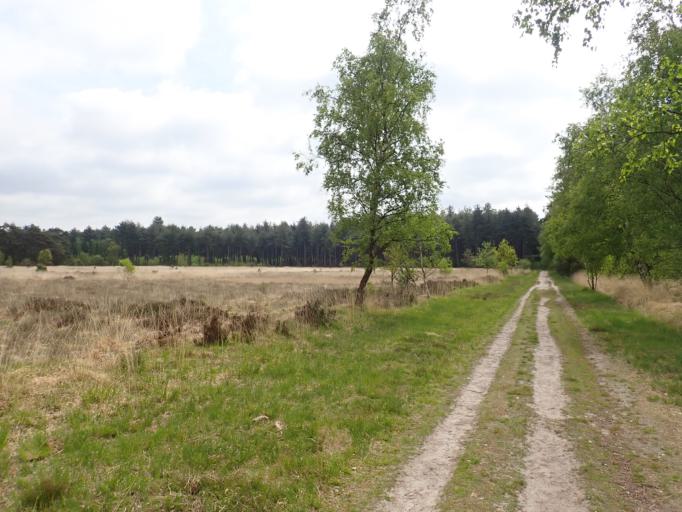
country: BE
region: Flanders
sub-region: Provincie Antwerpen
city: Kalmthout
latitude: 51.3779
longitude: 4.4421
